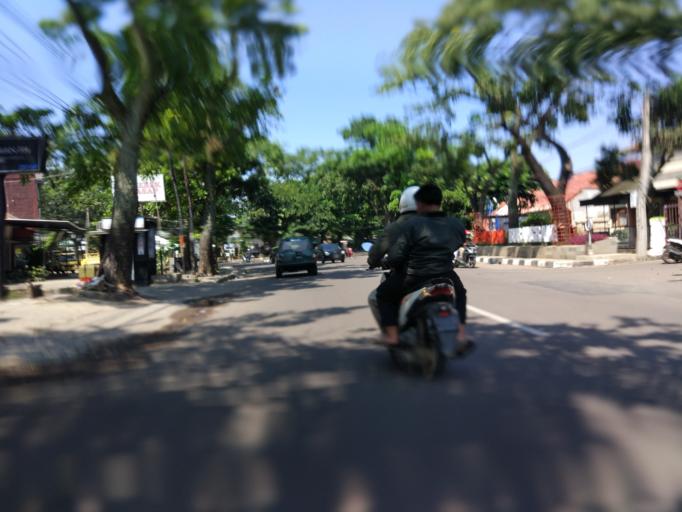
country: ID
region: West Java
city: Bandung
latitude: -6.9292
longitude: 107.6196
